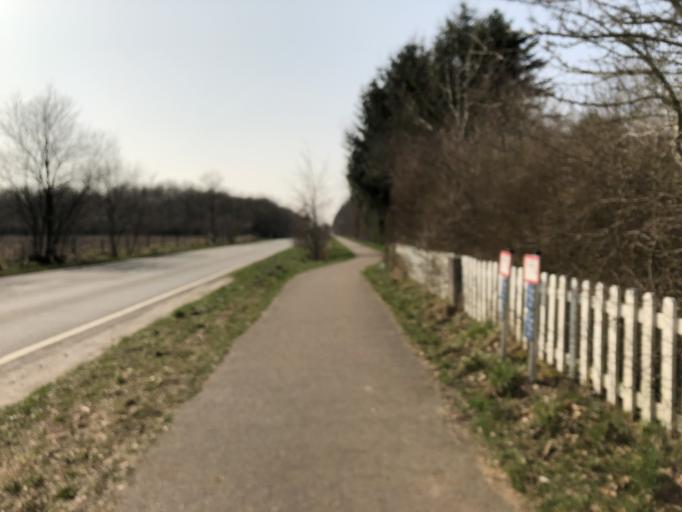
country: DE
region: Schleswig-Holstein
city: Tarp
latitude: 54.6581
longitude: 9.3909
